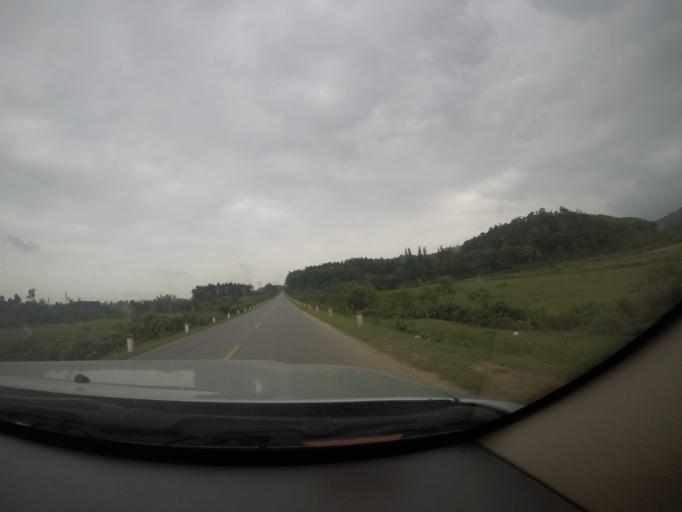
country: VN
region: Quang Binh
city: Hoan Lao
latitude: 17.6146
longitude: 106.3964
